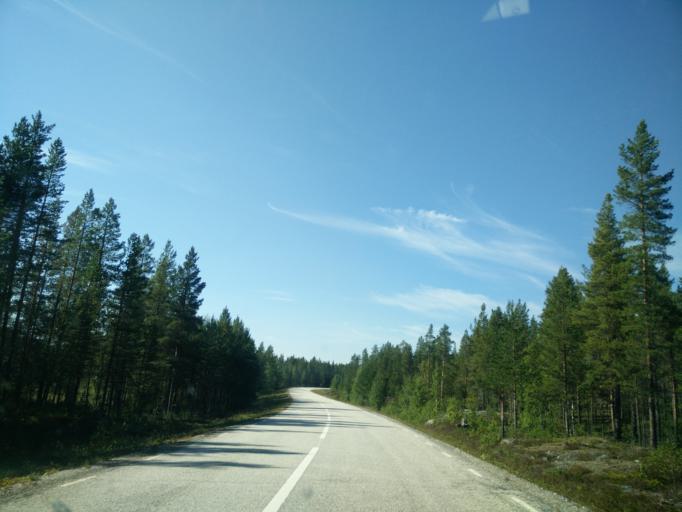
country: SE
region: Jaemtland
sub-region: Are Kommun
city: Jarpen
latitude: 62.8286
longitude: 13.4606
